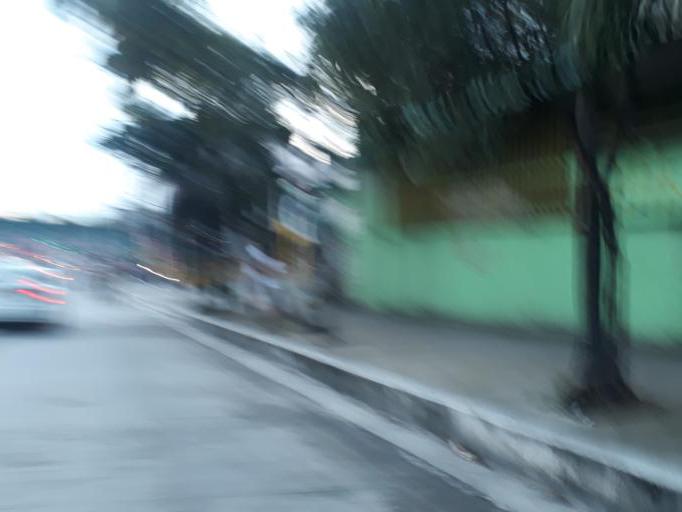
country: PH
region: Metro Manila
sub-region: Quezon City
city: Quezon City
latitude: 14.6670
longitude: 121.0722
